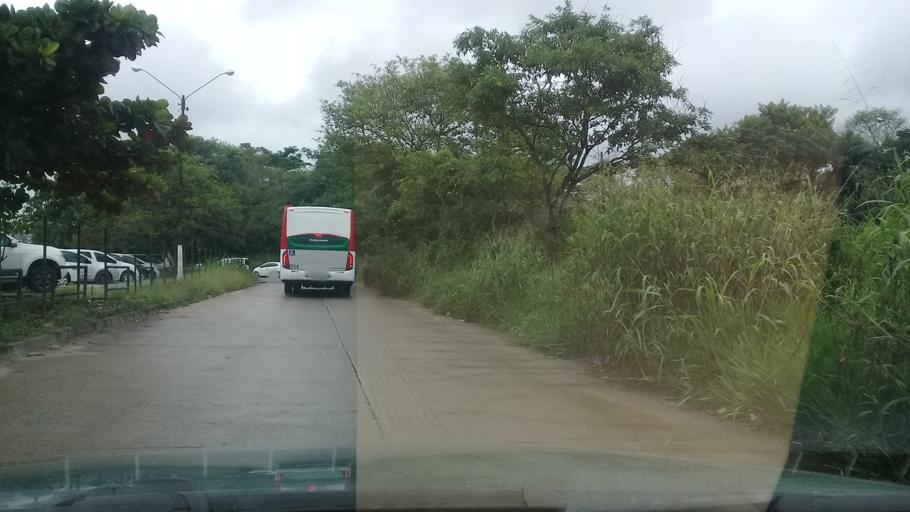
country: BR
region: Pernambuco
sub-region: Jaboatao Dos Guararapes
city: Jaboatao dos Guararapes
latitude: -8.0630
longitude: -34.9826
